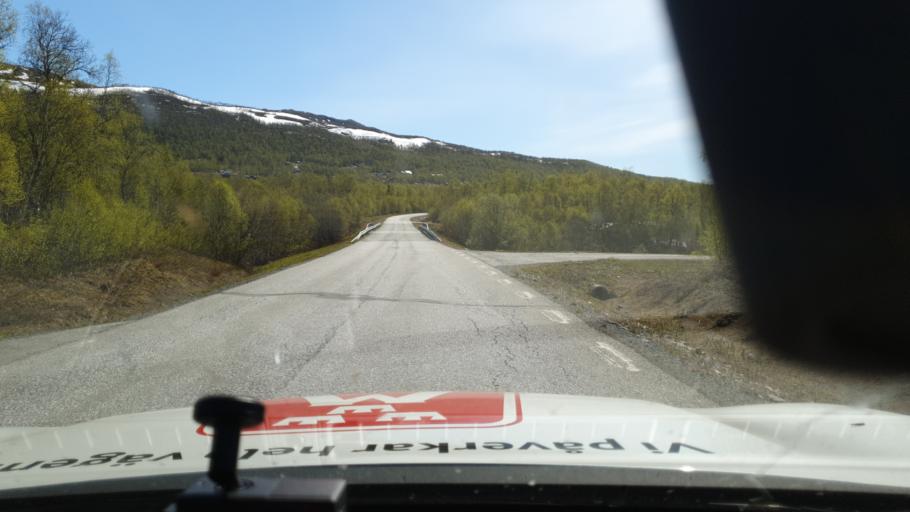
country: NO
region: Nordland
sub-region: Rana
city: Mo i Rana
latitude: 65.7813
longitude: 15.1220
